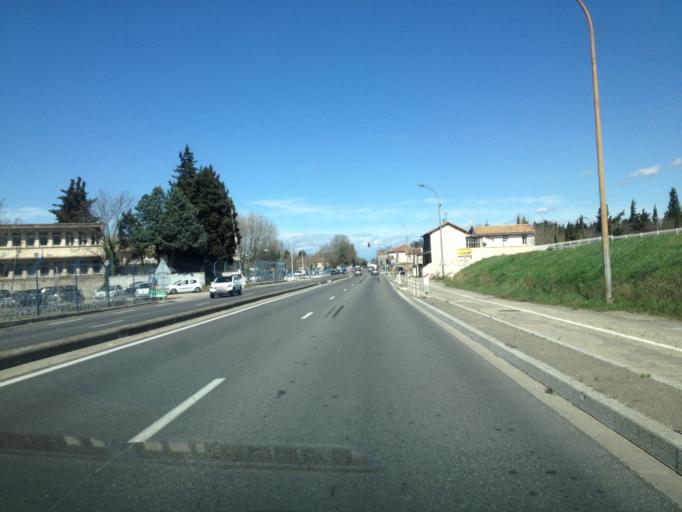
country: FR
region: Provence-Alpes-Cote d'Azur
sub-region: Departement du Vaucluse
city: Sorgues
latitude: 43.9910
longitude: 4.8636
